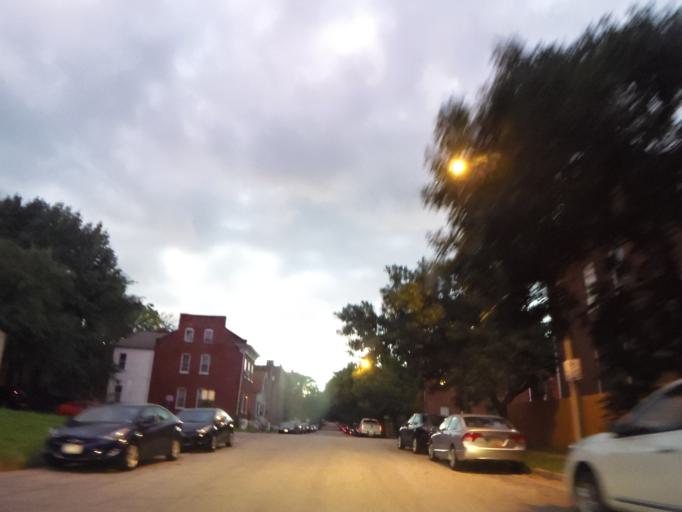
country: US
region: Missouri
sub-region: City of Saint Louis
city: St. Louis
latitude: 38.6029
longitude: -90.2077
